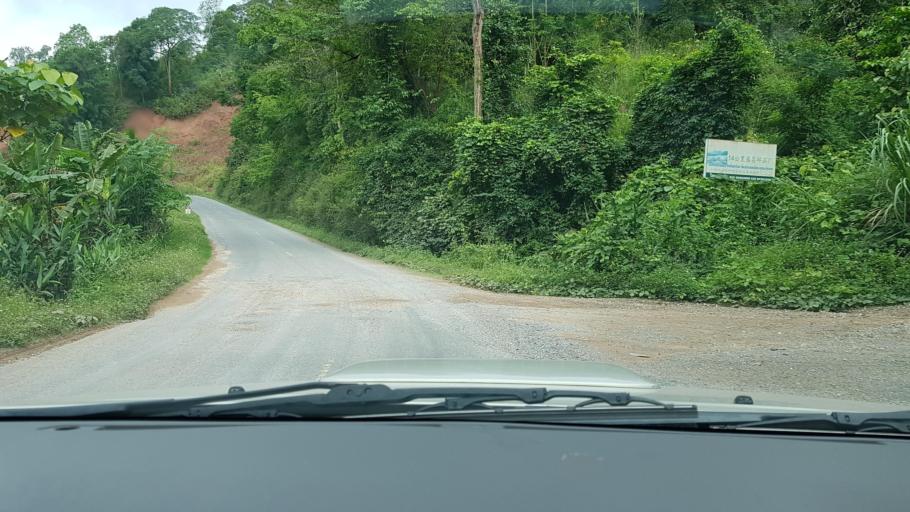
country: LA
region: Oudomxai
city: Muang Xay
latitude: 20.5947
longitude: 101.9369
